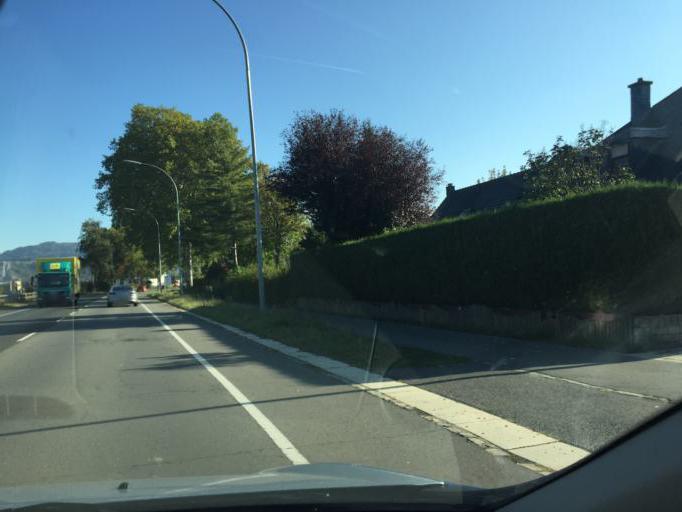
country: LU
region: Diekirch
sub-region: Canton de Diekirch
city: Diekirch
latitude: 49.8567
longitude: 6.1369
